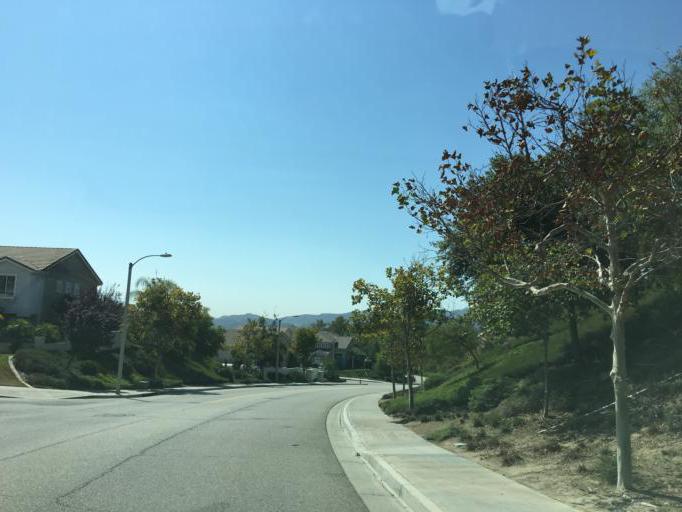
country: US
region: California
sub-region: Los Angeles County
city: Santa Clarita
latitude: 34.3927
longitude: -118.5902
